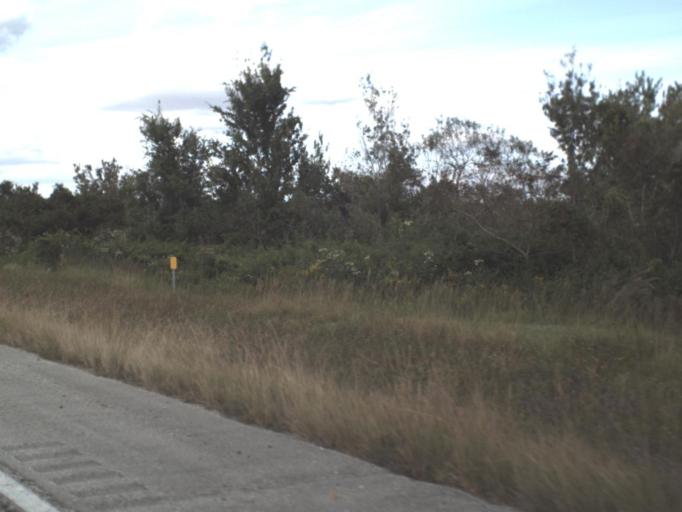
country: US
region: Florida
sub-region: Brevard County
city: Port Saint John
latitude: 28.4271
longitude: -80.8514
